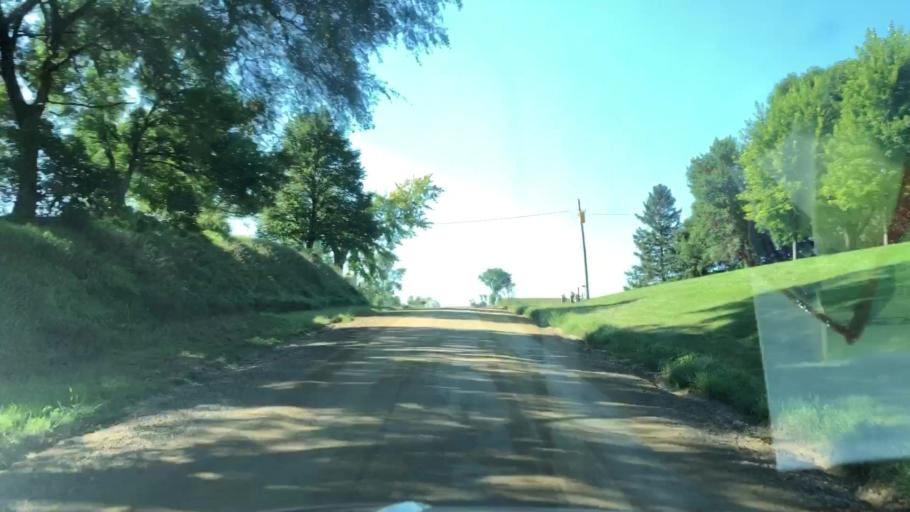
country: US
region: Iowa
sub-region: Woodbury County
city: Sergeant Bluff
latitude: 42.4709
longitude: -96.2522
